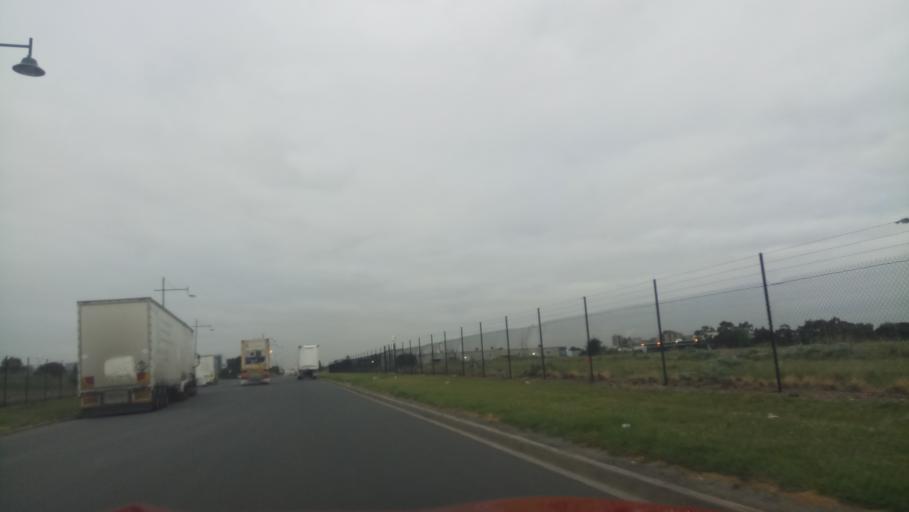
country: AU
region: Victoria
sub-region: Hobsons Bay
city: Laverton
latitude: -37.8539
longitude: 144.7891
